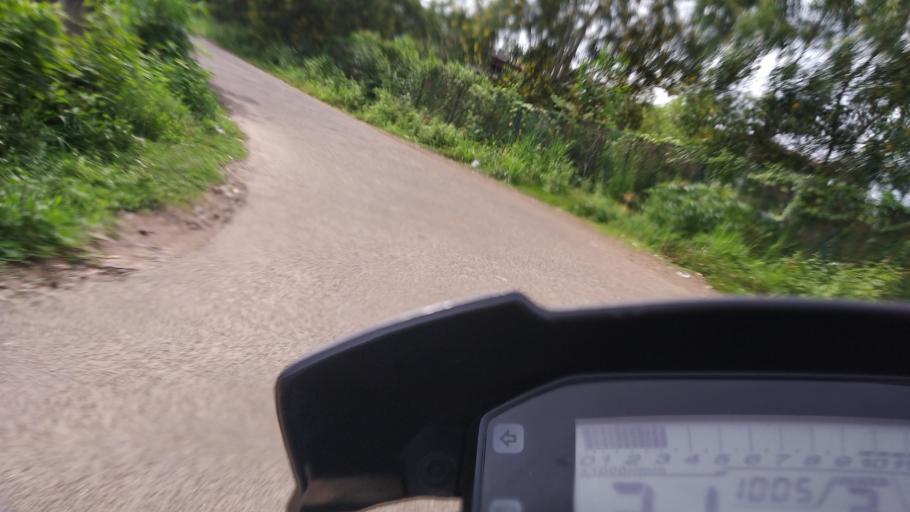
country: IN
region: Kerala
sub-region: Ernakulam
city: Aluva
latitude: 10.0563
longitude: 76.3523
